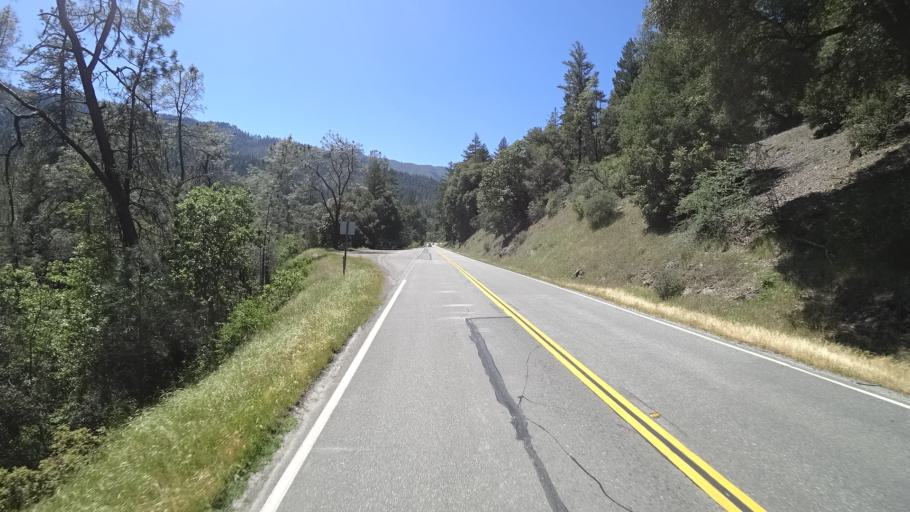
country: US
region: California
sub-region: Trinity County
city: Hayfork
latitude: 40.7419
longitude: -123.2596
